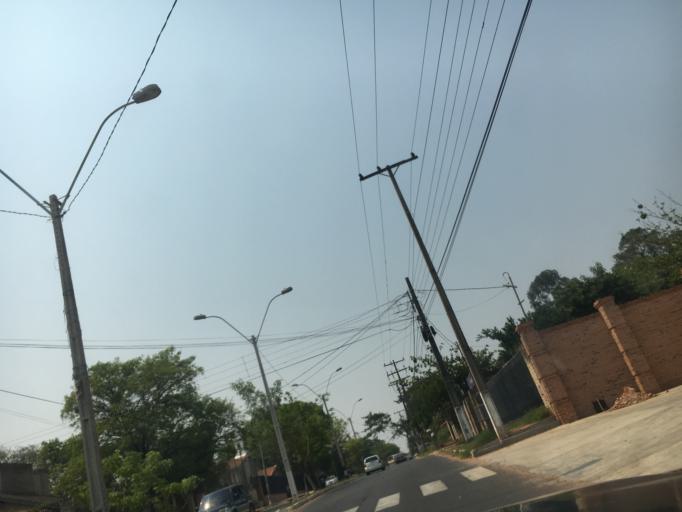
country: PY
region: Central
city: Villa Elisa
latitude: -25.3790
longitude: -57.5894
